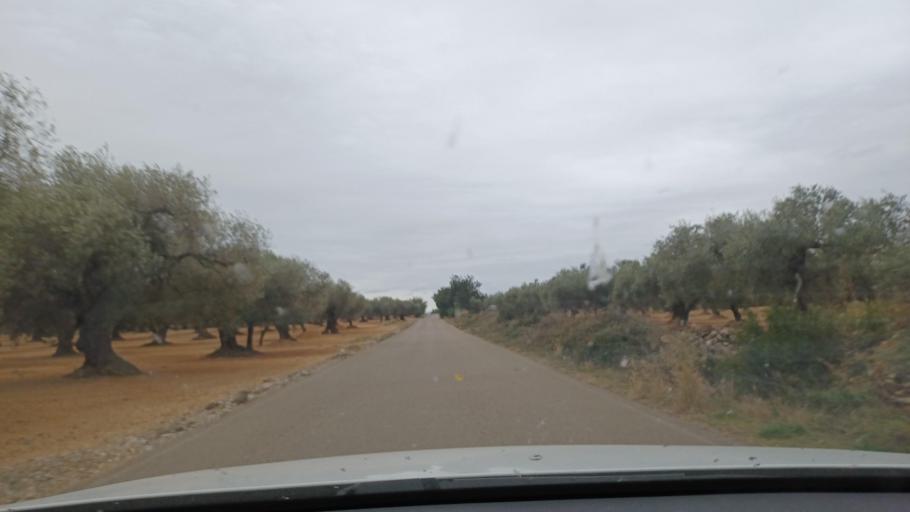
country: ES
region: Valencia
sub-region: Provincia de Castello
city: Canet lo Roig
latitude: 40.5755
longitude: 0.2802
